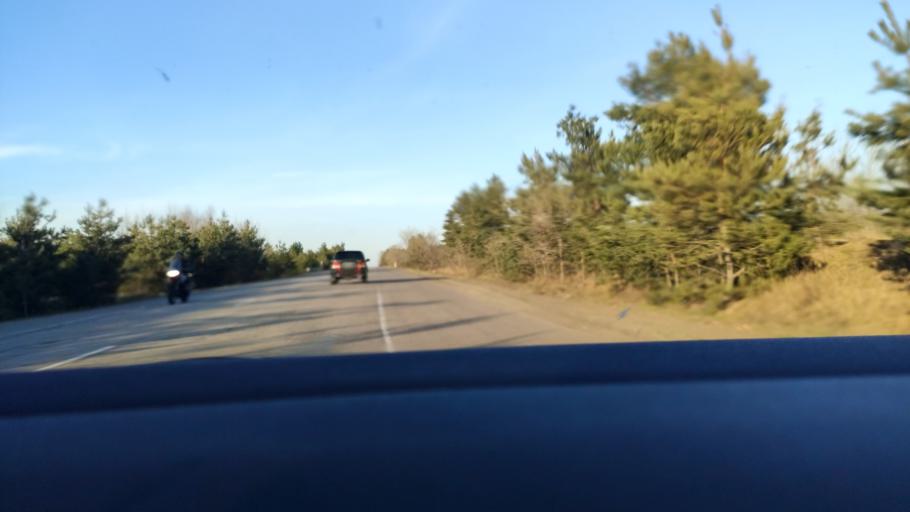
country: RU
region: Voronezj
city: Kolodeznyy
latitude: 51.3616
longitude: 39.1873
